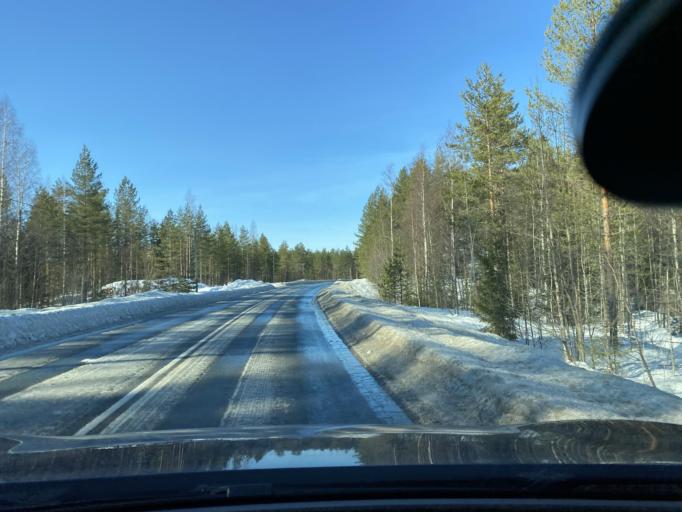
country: FI
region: Central Finland
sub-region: Joutsa
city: Joutsa
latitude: 61.7887
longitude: 26.0244
